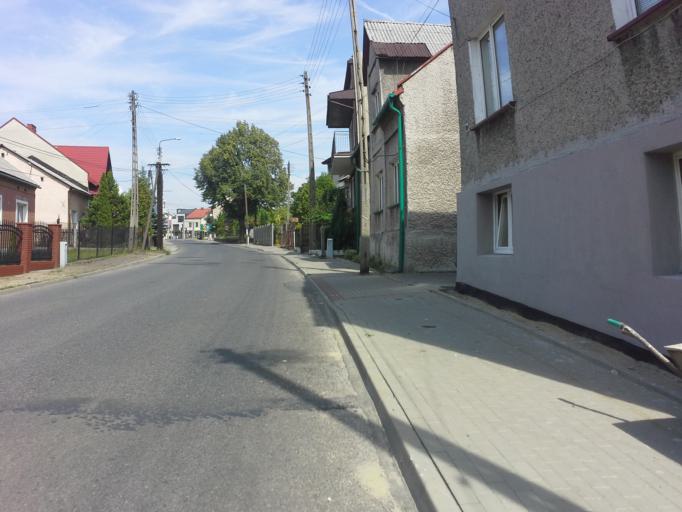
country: PL
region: Lesser Poland Voivodeship
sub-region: Powiat chrzanowski
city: Trzebinia
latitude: 50.1564
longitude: 19.4721
